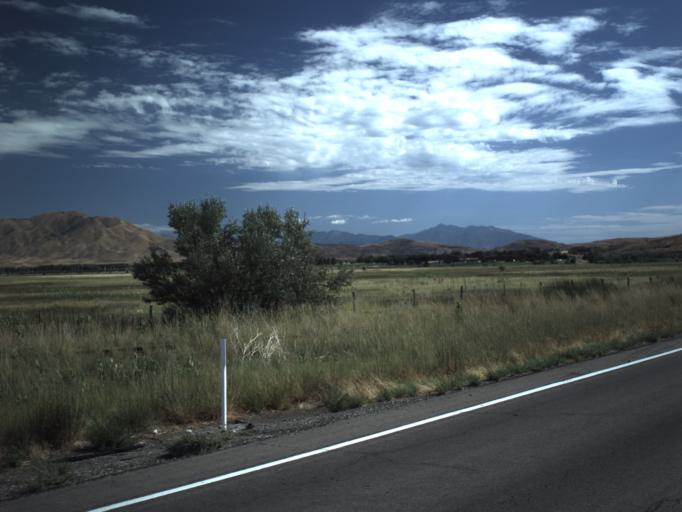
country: US
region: Utah
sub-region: Utah County
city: Genola
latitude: 39.9597
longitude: -111.8690
